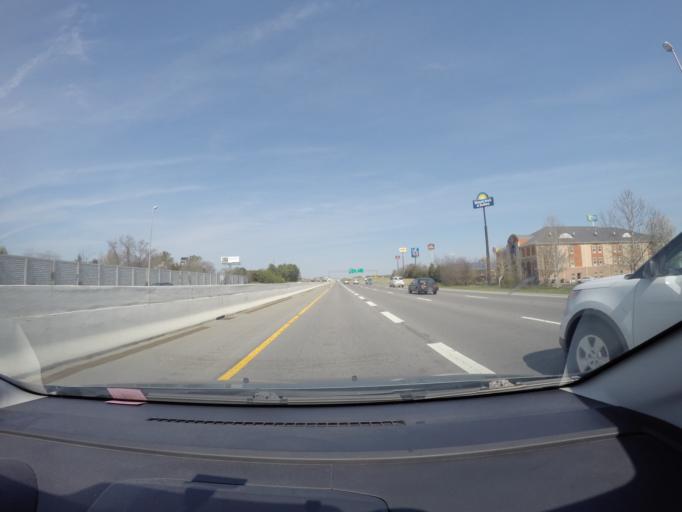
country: US
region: Tennessee
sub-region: Rutherford County
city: Murfreesboro
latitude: 35.8427
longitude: -86.4301
